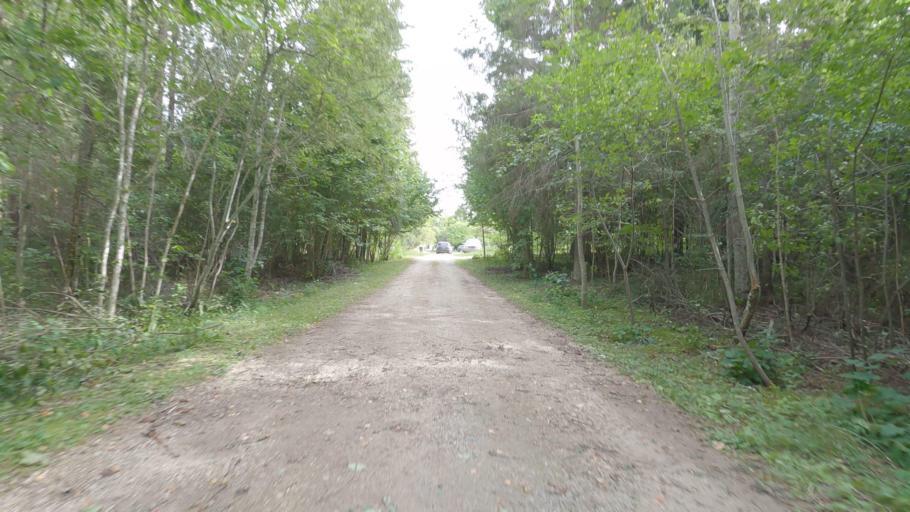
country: EE
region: Raplamaa
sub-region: Rapla vald
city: Rapla
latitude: 58.9896
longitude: 24.7928
